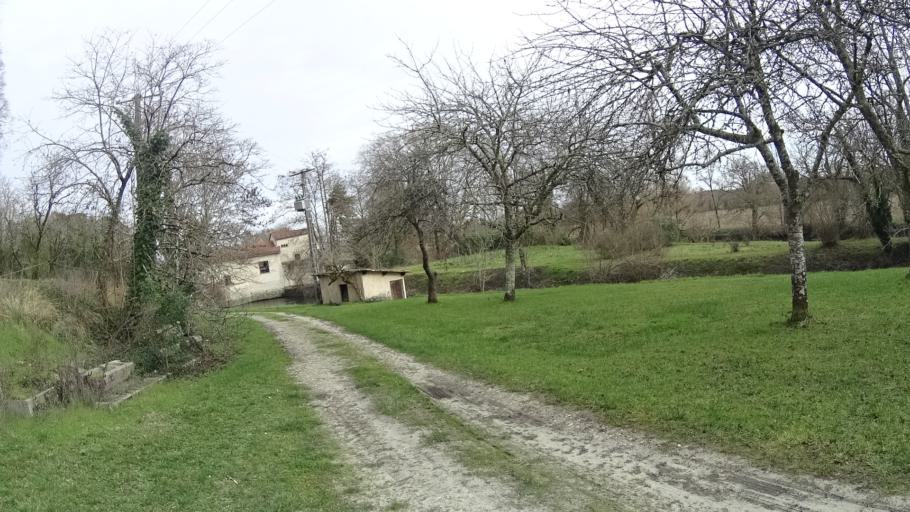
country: FR
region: Aquitaine
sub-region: Departement de la Dordogne
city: Saint-Aulaye
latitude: 45.2520
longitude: 0.1577
